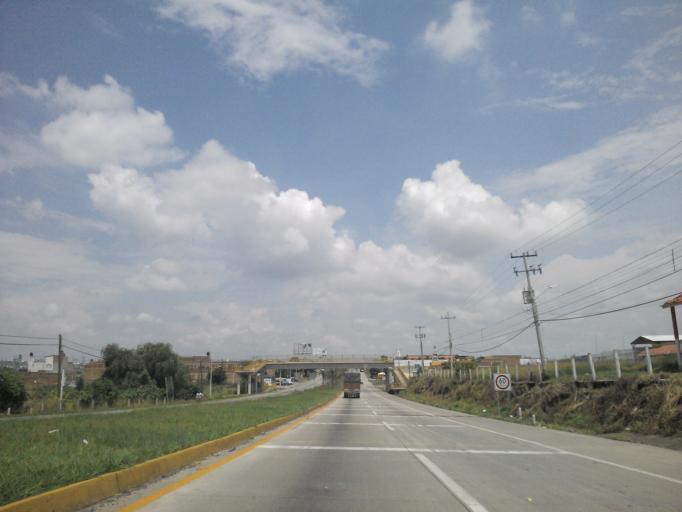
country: MX
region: Jalisco
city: Zapotlanejo
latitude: 20.6086
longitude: -103.0881
